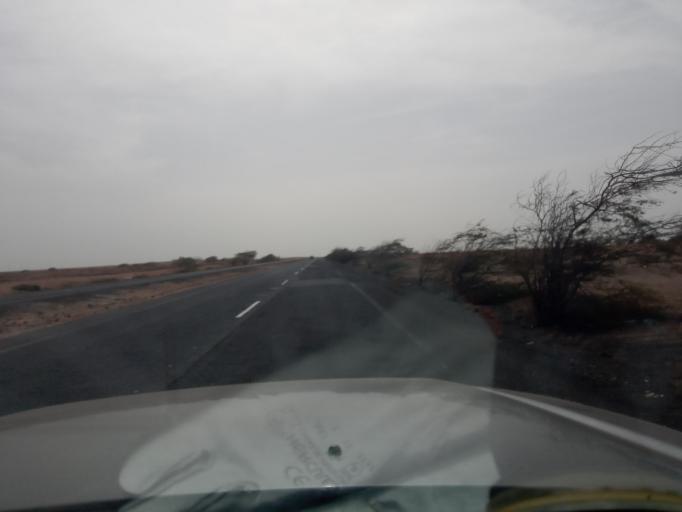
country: CV
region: Sal
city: Espargos
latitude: 16.7283
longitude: -22.9415
